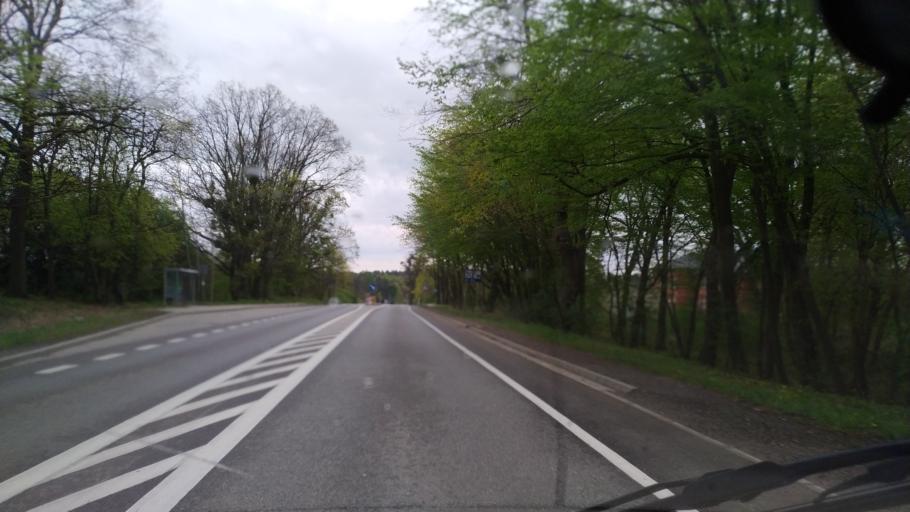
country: PL
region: Pomeranian Voivodeship
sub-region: Powiat tczewski
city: Subkowy
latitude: 54.0417
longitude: 18.6995
